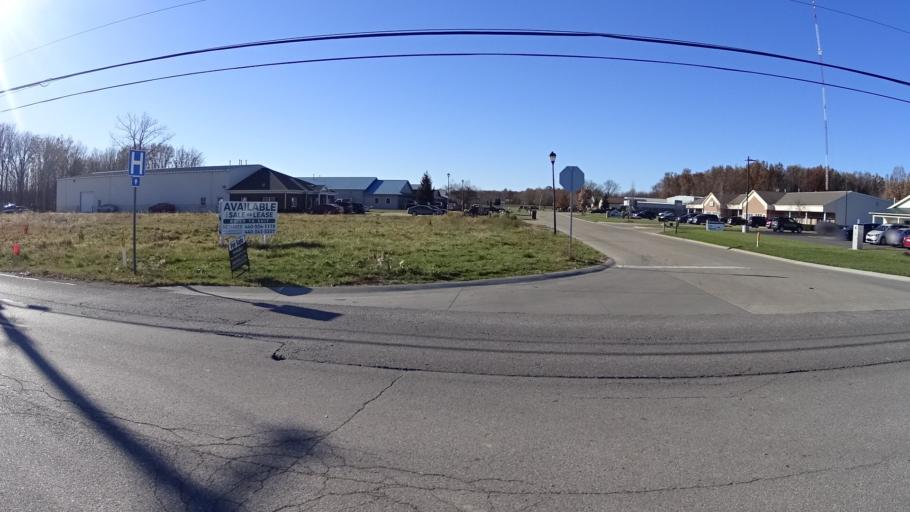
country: US
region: Ohio
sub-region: Lorain County
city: Avon Center
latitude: 41.4735
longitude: -81.9887
